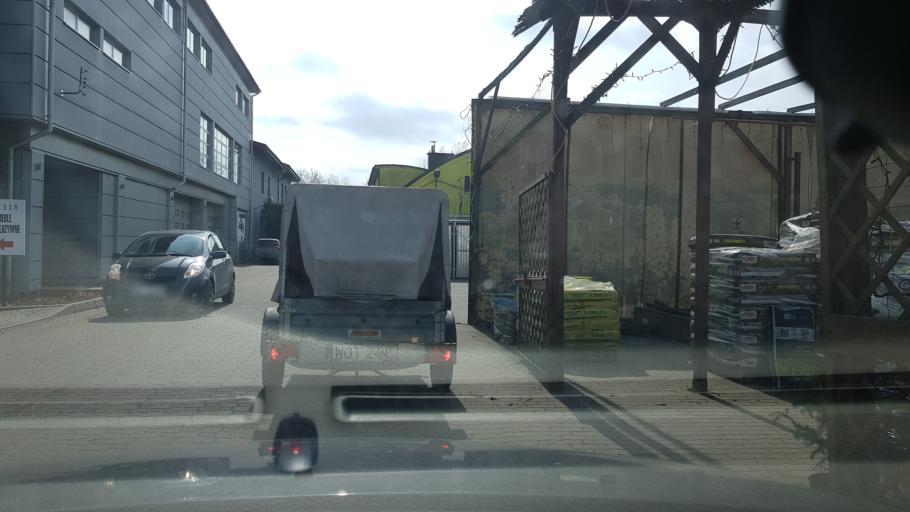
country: PL
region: Masovian Voivodeship
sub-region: Warszawa
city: Wesola
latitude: 52.2246
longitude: 21.2358
